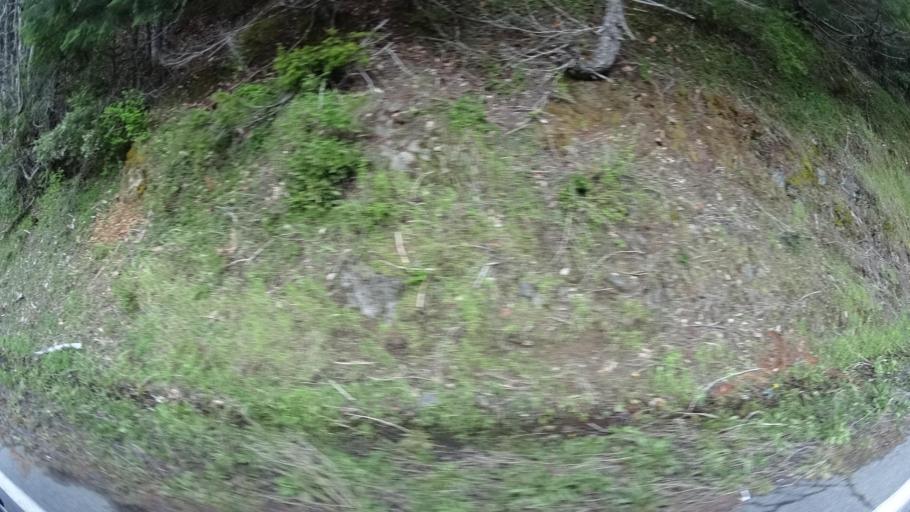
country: US
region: California
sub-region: Humboldt County
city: Willow Creek
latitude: 40.8952
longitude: -123.7693
